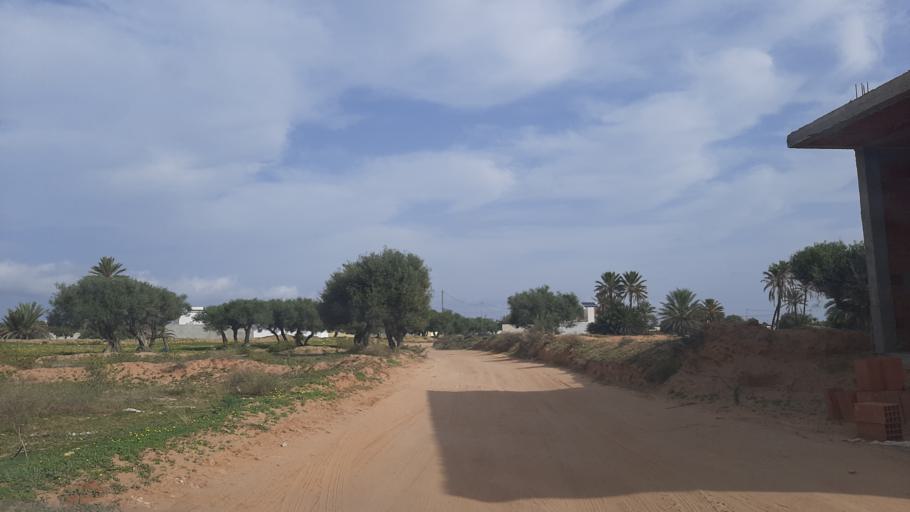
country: TN
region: Madanin
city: Midoun
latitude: 33.8090
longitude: 11.0243
